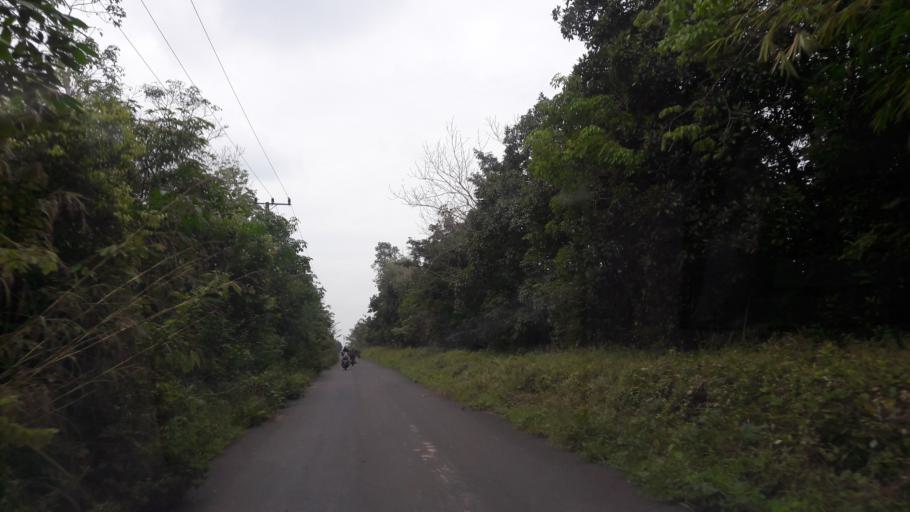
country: ID
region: South Sumatra
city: Gunungmenang
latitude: -3.2187
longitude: 104.0382
